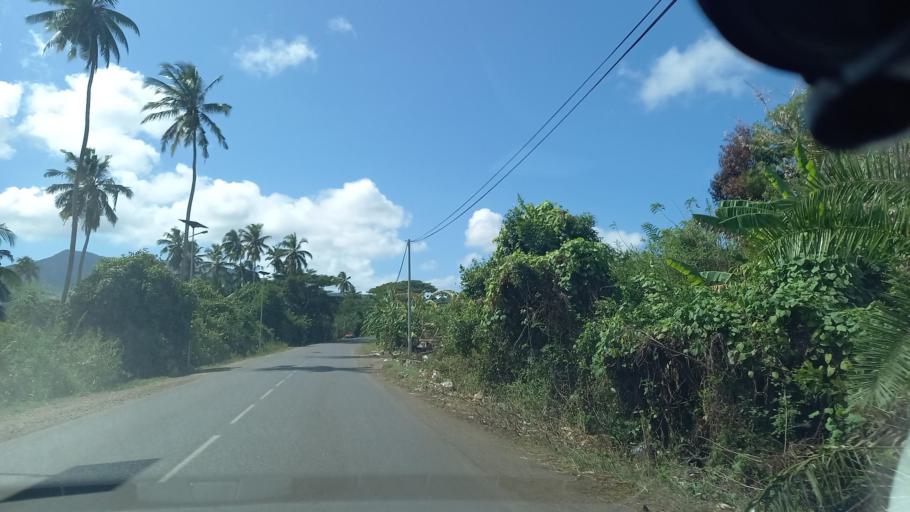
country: YT
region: Chirongui
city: Chirongui
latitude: -12.9266
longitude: 45.1541
